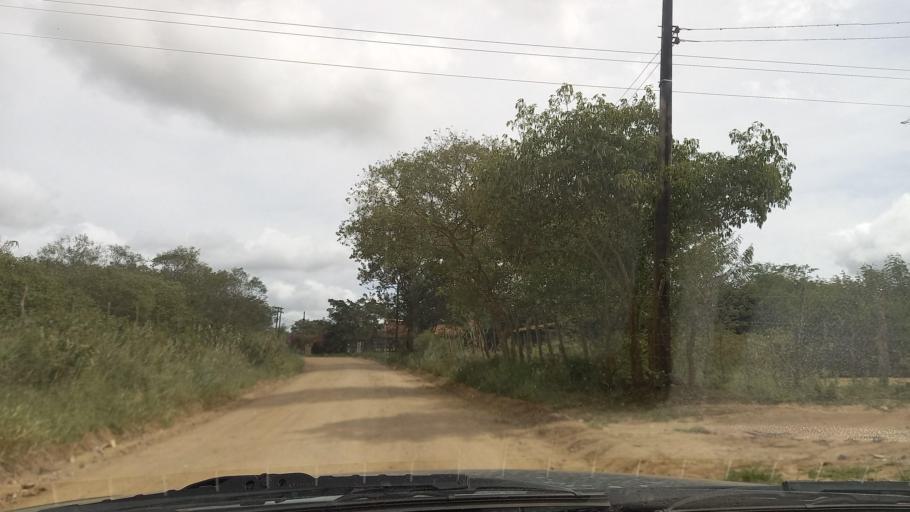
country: BR
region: Pernambuco
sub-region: Gravata
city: Gravata
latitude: -8.1811
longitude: -35.5891
